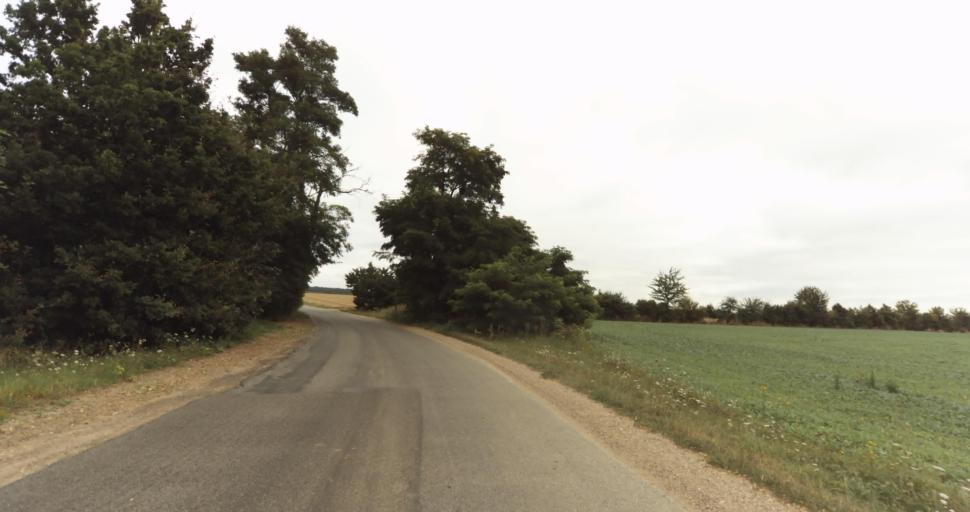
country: FR
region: Centre
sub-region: Departement d'Eure-et-Loir
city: Saint-Lubin-des-Joncherets
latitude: 48.7748
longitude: 1.2162
